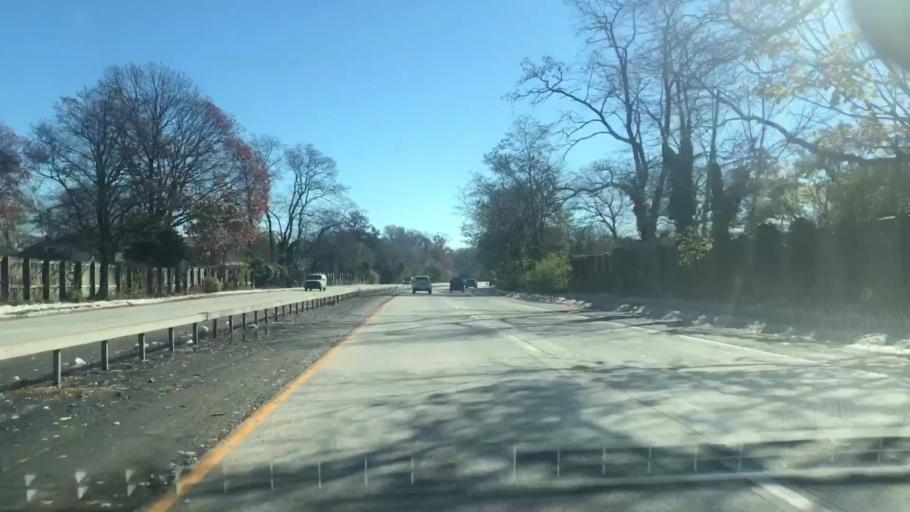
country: US
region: New York
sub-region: Suffolk County
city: North Babylon
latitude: 40.7259
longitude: -73.3177
